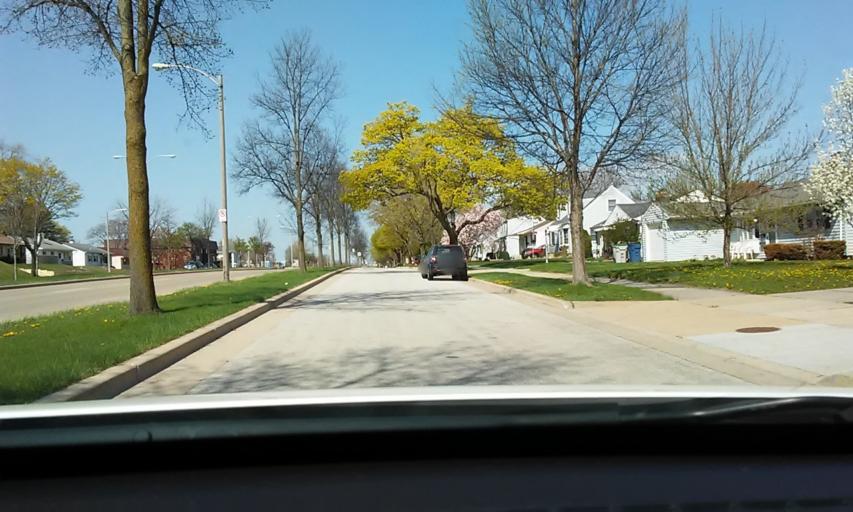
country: US
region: Wisconsin
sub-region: Milwaukee County
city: West Allis
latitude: 42.9886
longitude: -87.9932
